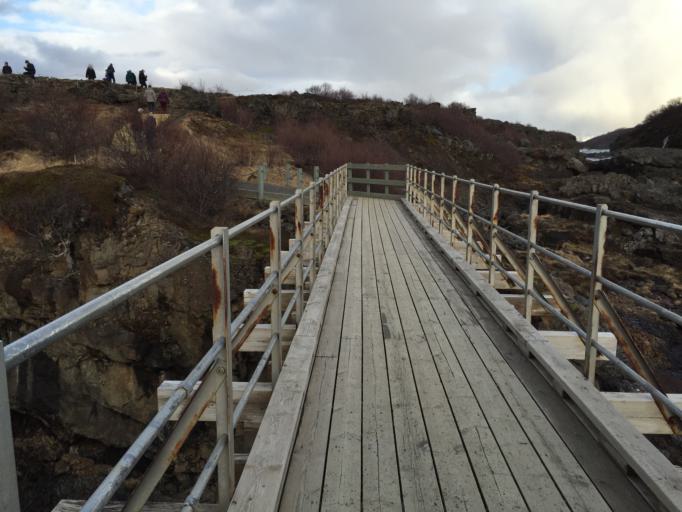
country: IS
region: South
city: Hveragerdi
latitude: 64.7020
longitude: -20.9746
